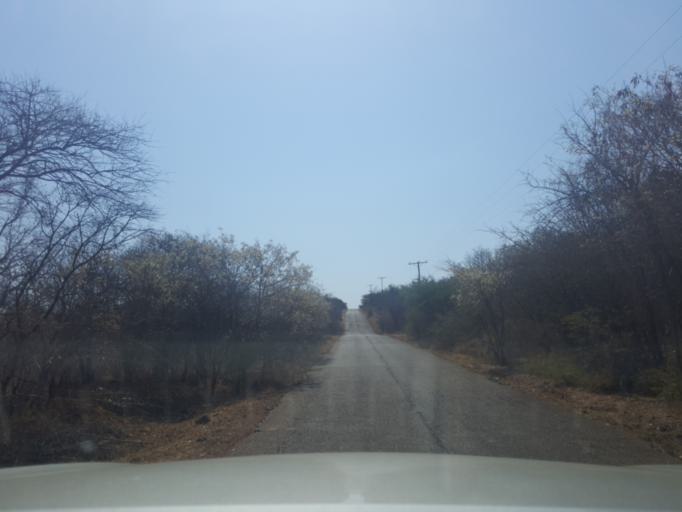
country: BW
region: Kweneng
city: Gabane
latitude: -24.7417
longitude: 25.8220
